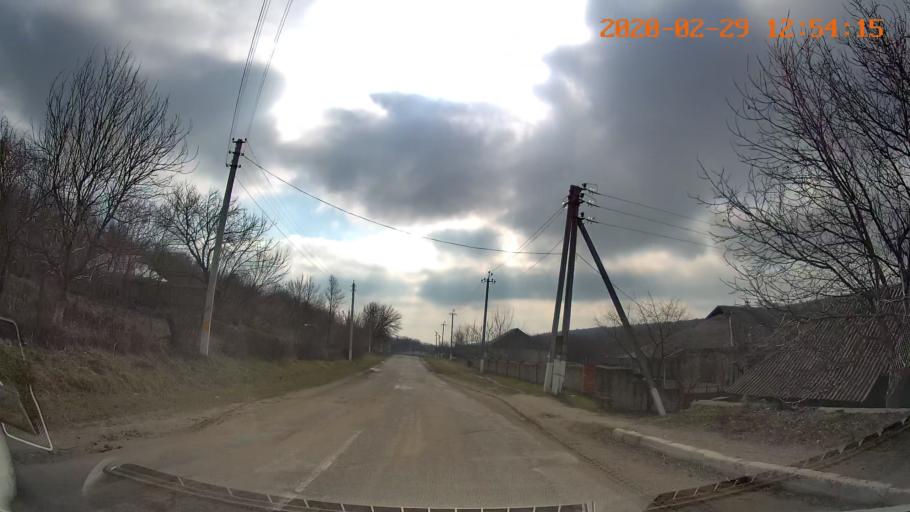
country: MD
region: Telenesti
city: Camenca
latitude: 48.1035
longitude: 28.7278
